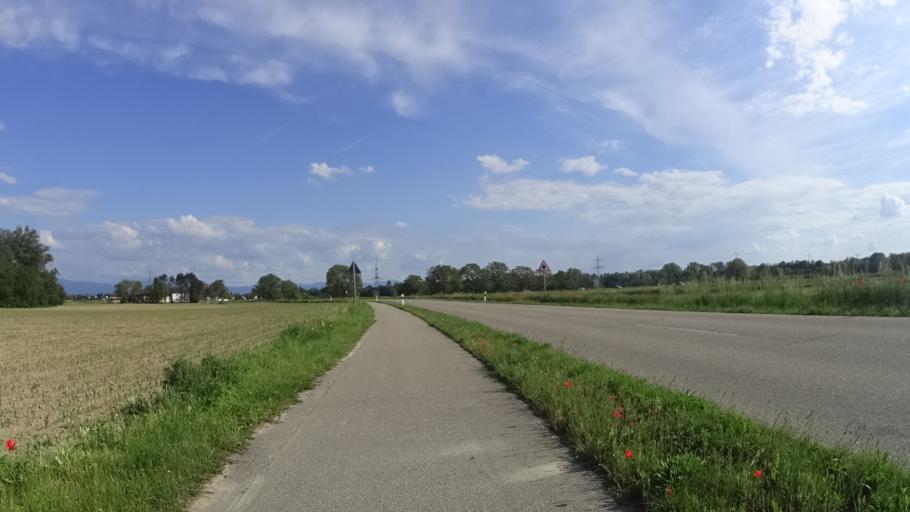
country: DE
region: Baden-Wuerttemberg
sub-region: Freiburg Region
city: Breisach am Rhein
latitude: 48.0273
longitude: 7.6012
